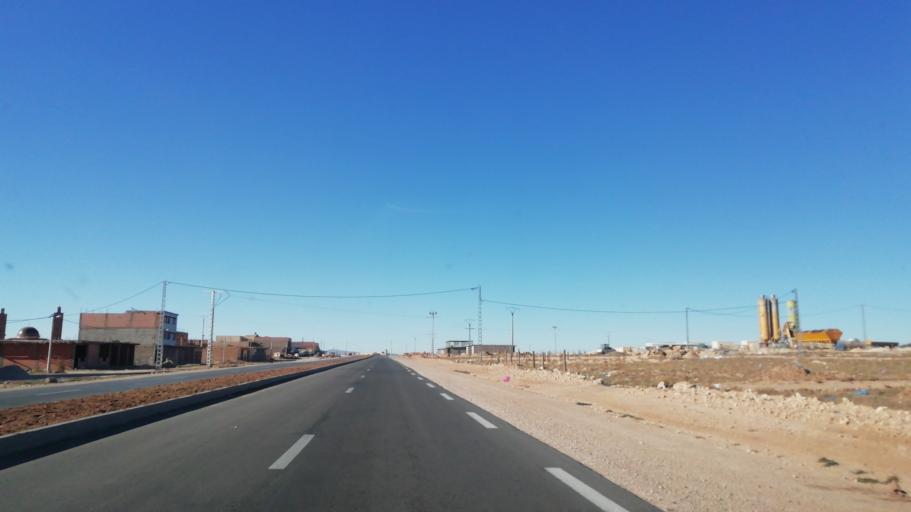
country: DZ
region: Tlemcen
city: Sebdou
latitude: 34.2178
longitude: -1.2471
